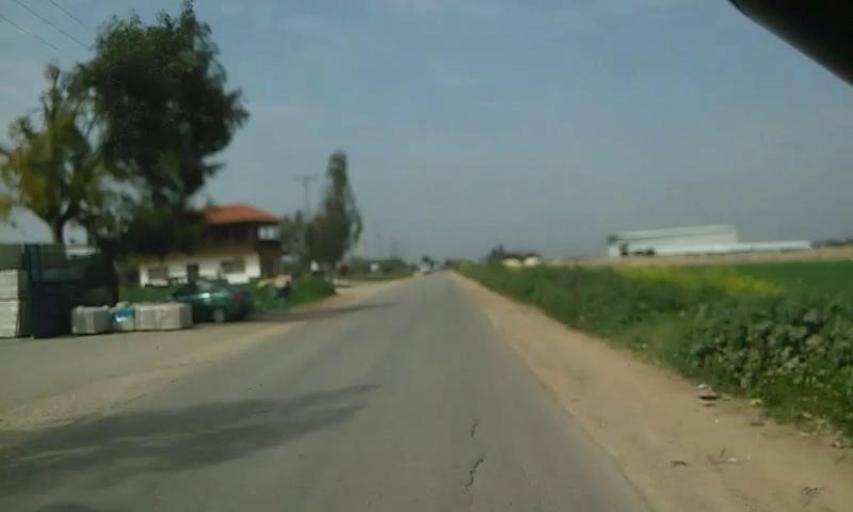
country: PS
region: West Bank
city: Kafr Dan
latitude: 32.4938
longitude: 35.2563
